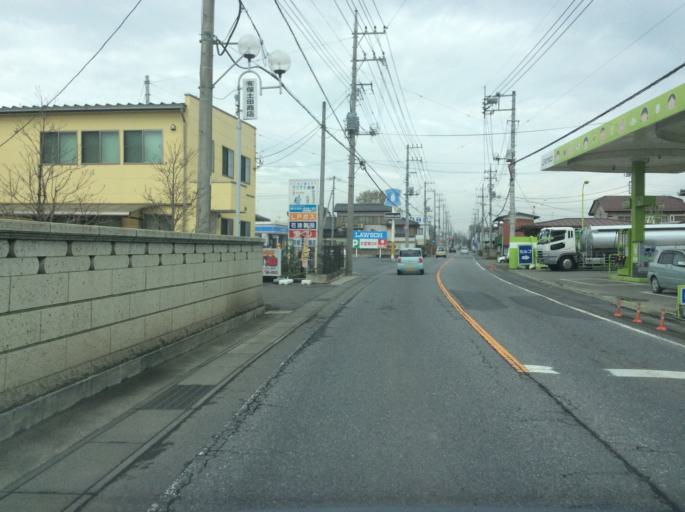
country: JP
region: Ibaraki
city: Iwai
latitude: 36.0082
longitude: 139.9048
